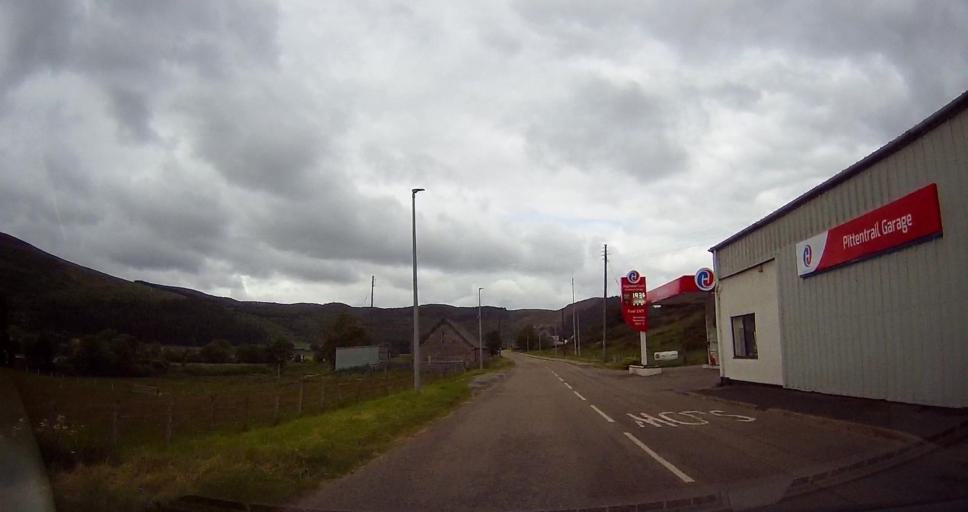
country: GB
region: Scotland
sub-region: Highland
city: Dornoch
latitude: 57.9896
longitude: -4.1565
